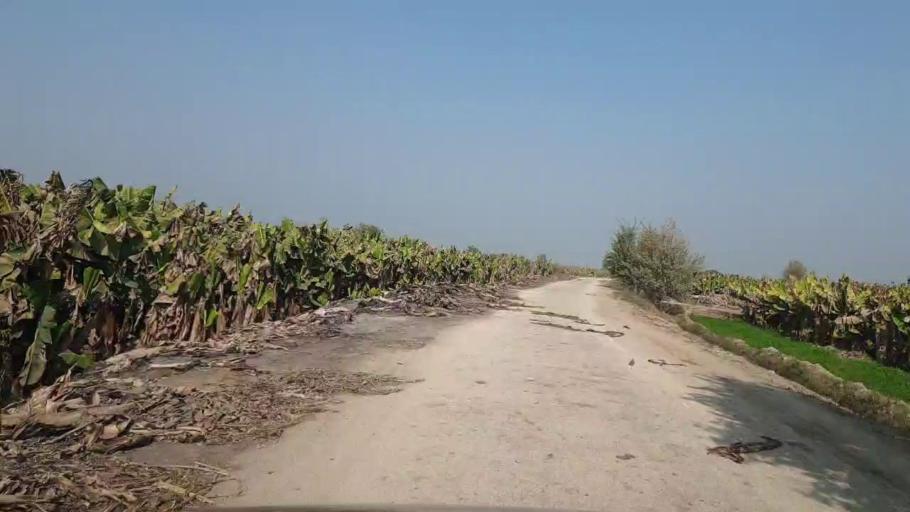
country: PK
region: Sindh
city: Bhit Shah
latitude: 25.7669
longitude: 68.4943
